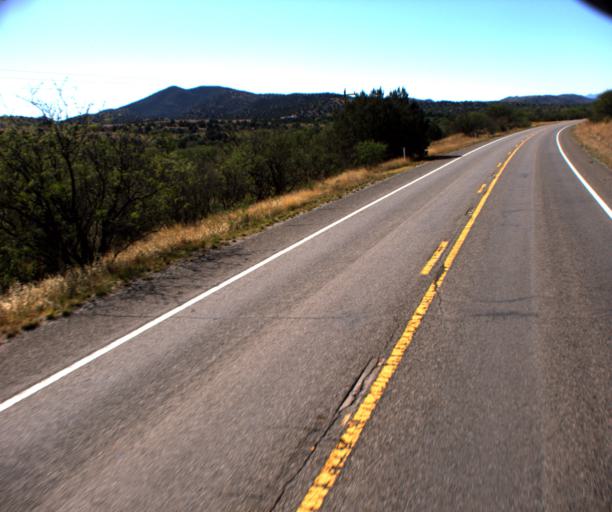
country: US
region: Arizona
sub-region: Santa Cruz County
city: Rio Rico
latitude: 31.6376
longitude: -110.7135
